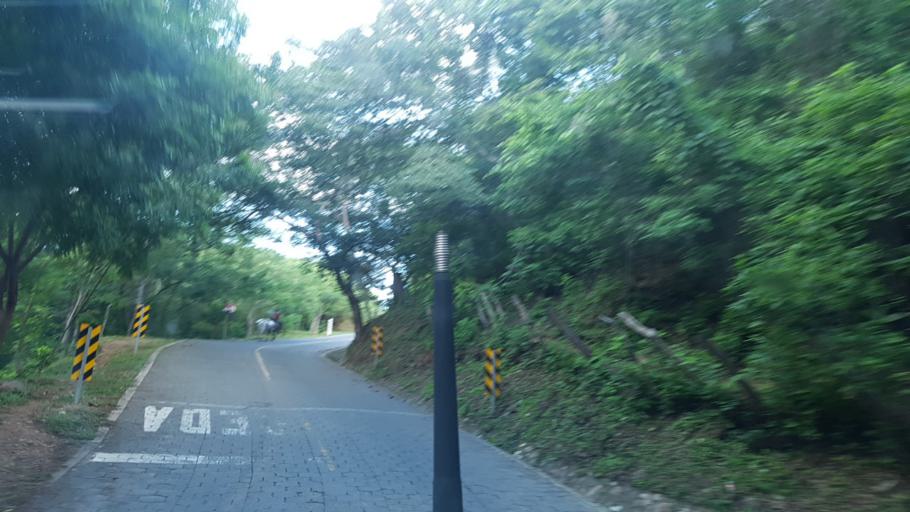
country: NI
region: Nueva Segovia
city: Ocotal
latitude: 13.6482
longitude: -86.6080
